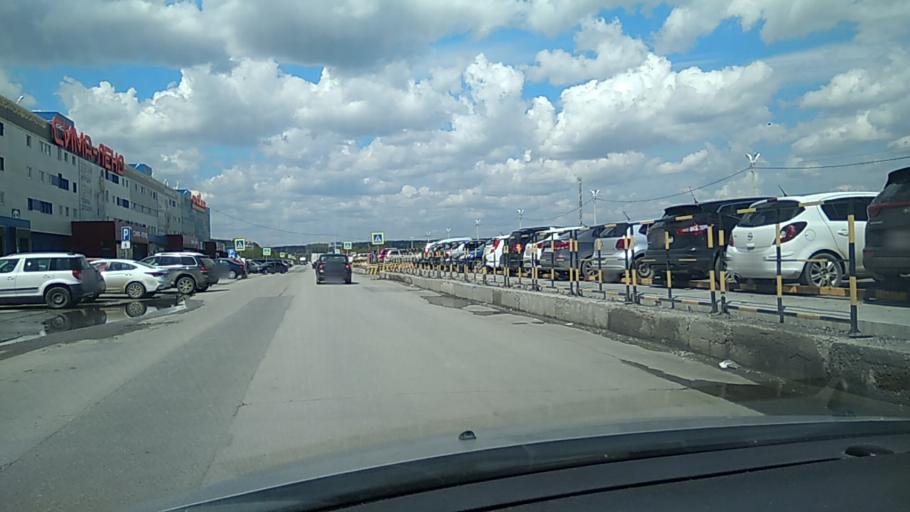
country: RU
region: Sverdlovsk
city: Istok
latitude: 56.7612
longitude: 60.7516
